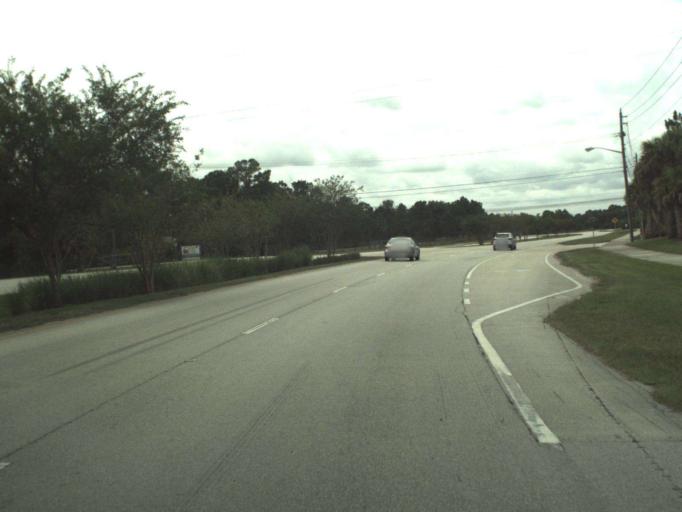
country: US
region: Florida
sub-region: Saint Lucie County
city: White City
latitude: 27.3542
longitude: -80.3562
